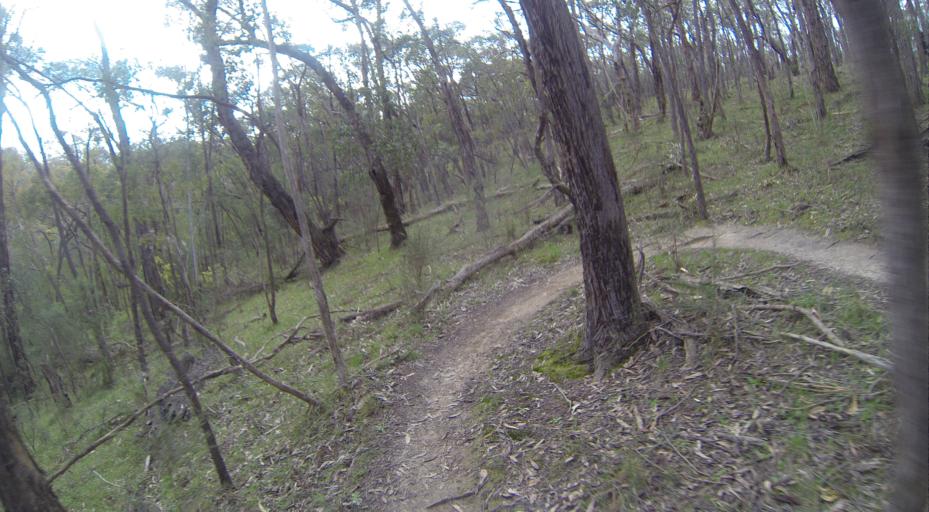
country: AU
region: Victoria
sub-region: Nillumbik
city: Saint Andrews
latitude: -37.6417
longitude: 145.2932
